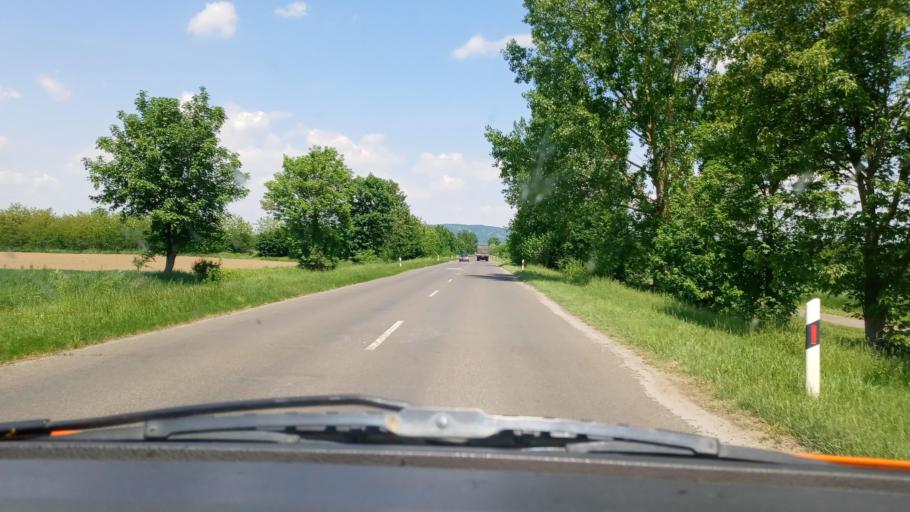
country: HU
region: Baranya
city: Harkany
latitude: 45.8273
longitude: 18.2216
